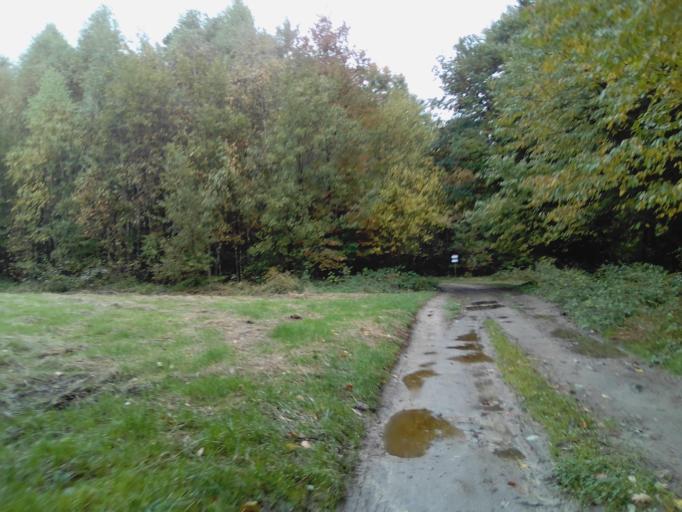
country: PL
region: Subcarpathian Voivodeship
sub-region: Powiat strzyzowski
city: Gwoznica Gorna
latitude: 49.8387
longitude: 22.0216
